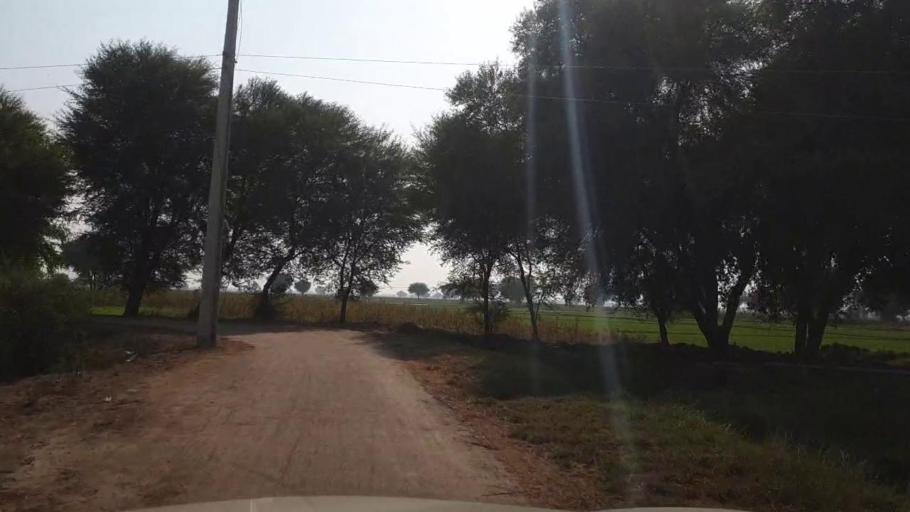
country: PK
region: Sindh
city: Bhan
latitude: 26.5412
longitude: 67.7516
